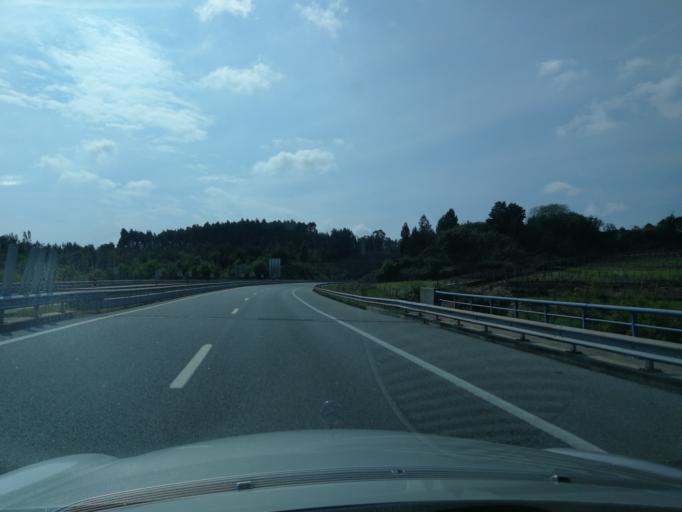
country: PT
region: Braga
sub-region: Vila Nova de Famalicao
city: Calendario
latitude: 41.3822
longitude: -8.5255
